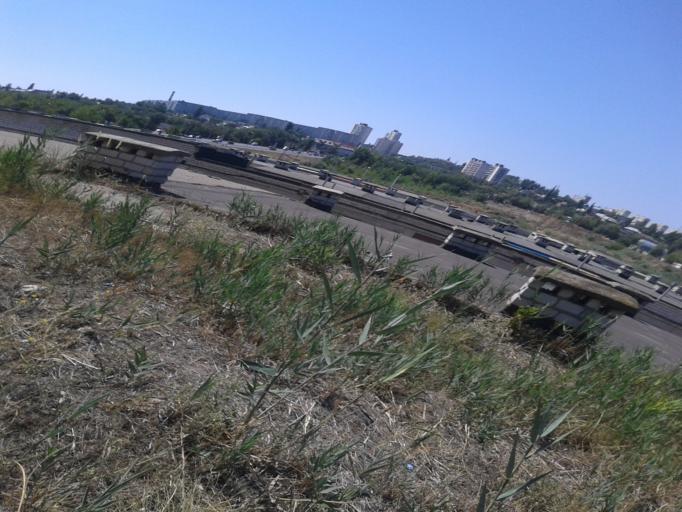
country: RU
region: Volgograd
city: Volgograd
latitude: 48.6883
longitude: 44.4526
